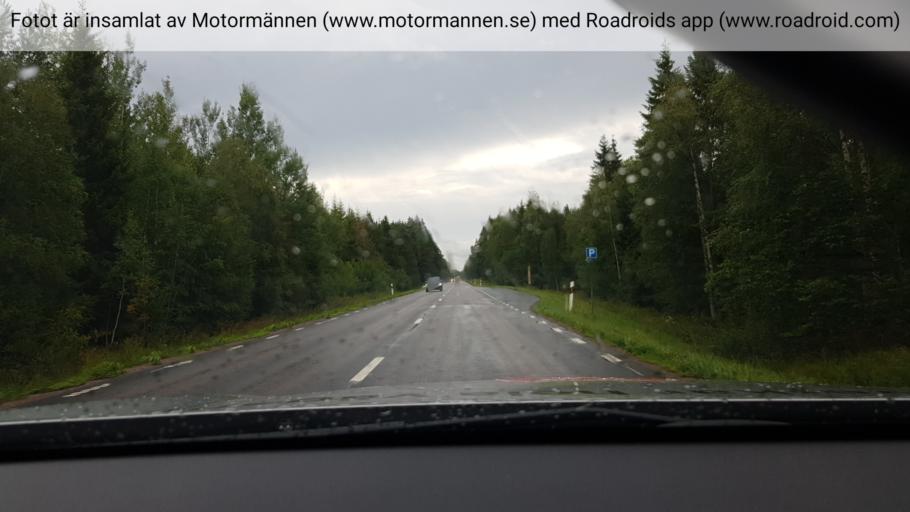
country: SE
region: Uppsala
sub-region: Tierps Kommun
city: Karlholmsbruk
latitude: 60.5296
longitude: 17.5912
